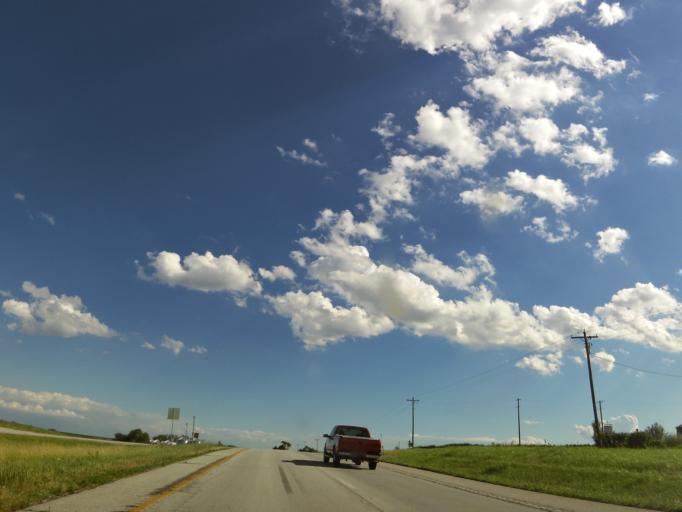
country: US
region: Missouri
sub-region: Marion County
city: Palmyra
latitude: 39.8674
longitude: -91.5255
